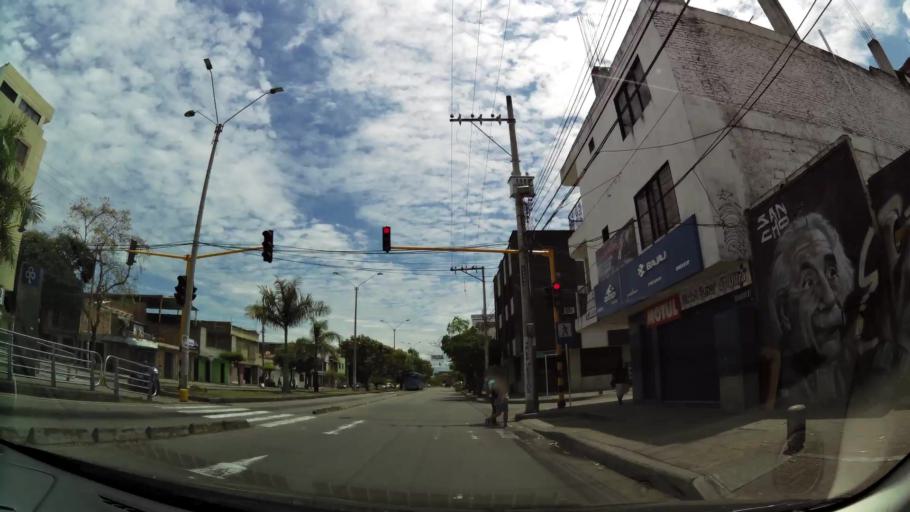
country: CO
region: Valle del Cauca
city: Cali
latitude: 3.4434
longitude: -76.4956
